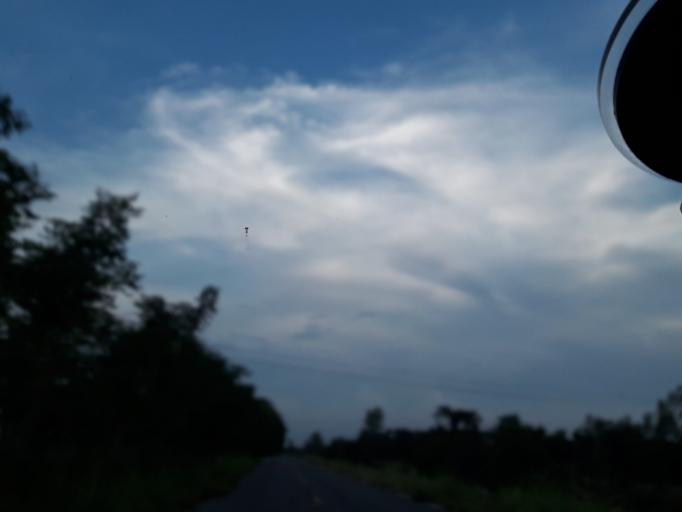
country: TH
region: Pathum Thani
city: Nong Suea
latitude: 14.2170
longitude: 100.8689
